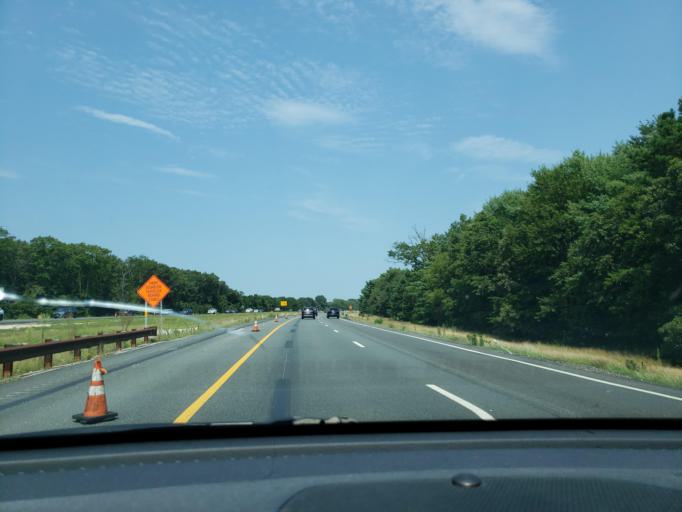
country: US
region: New Jersey
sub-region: Atlantic County
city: Linwood
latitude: 39.3716
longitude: -74.5835
